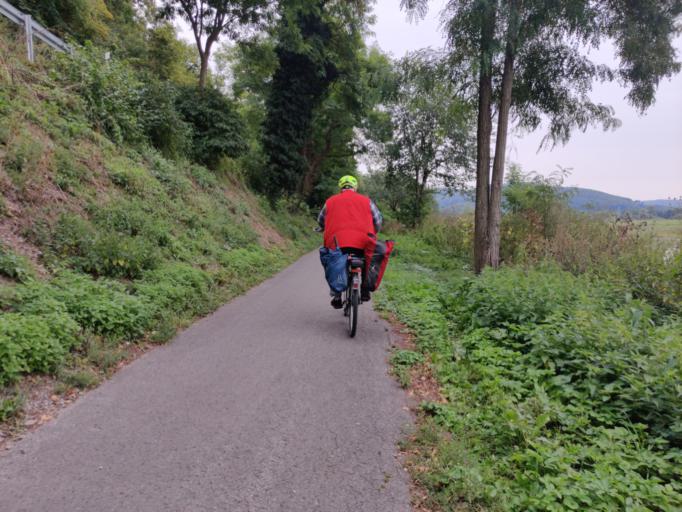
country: DE
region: Lower Saxony
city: Heinsen
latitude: 51.8868
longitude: 9.4557
